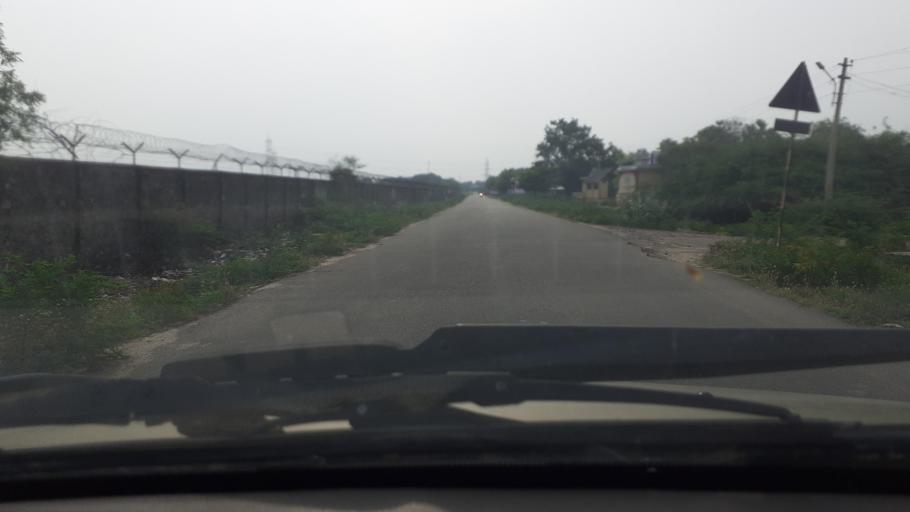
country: IN
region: Tamil Nadu
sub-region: Thoothukkudi
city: Korampallam
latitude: 8.7935
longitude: 78.1082
